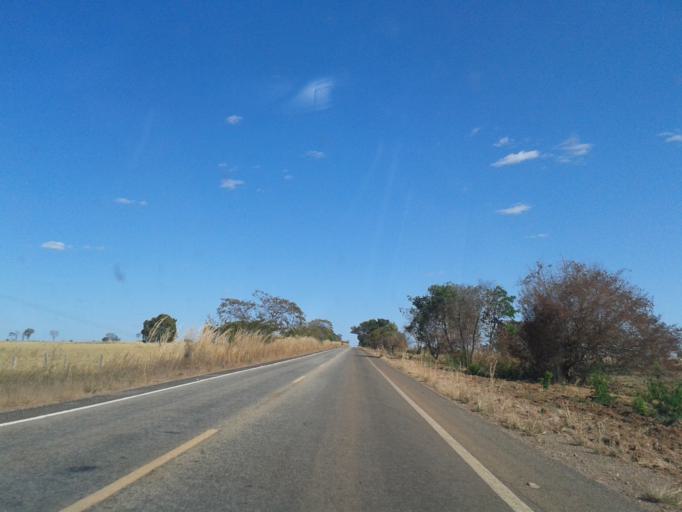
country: BR
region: Goias
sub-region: Mozarlandia
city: Mozarlandia
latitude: -14.5150
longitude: -50.4854
